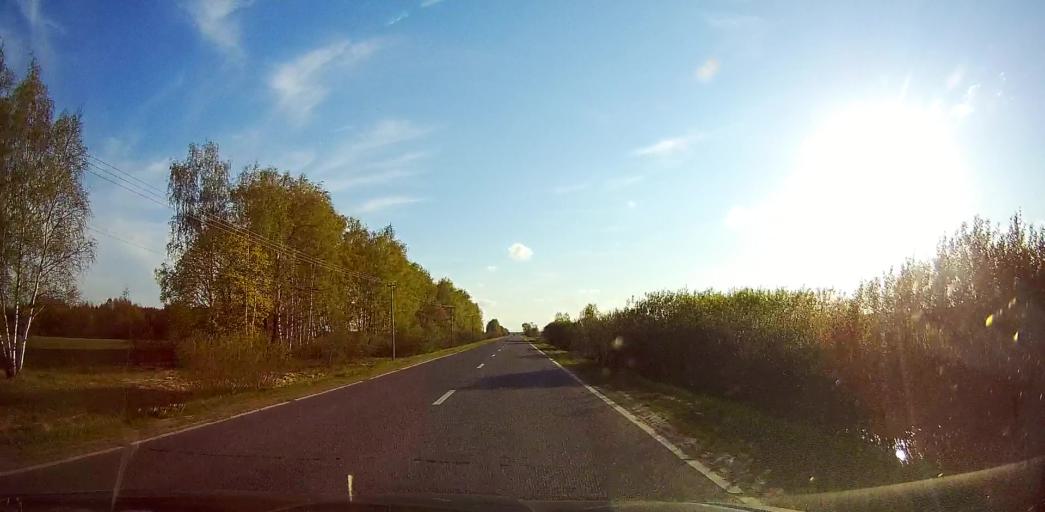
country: RU
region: Moskovskaya
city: Bronnitsy
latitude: 55.2888
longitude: 38.1925
